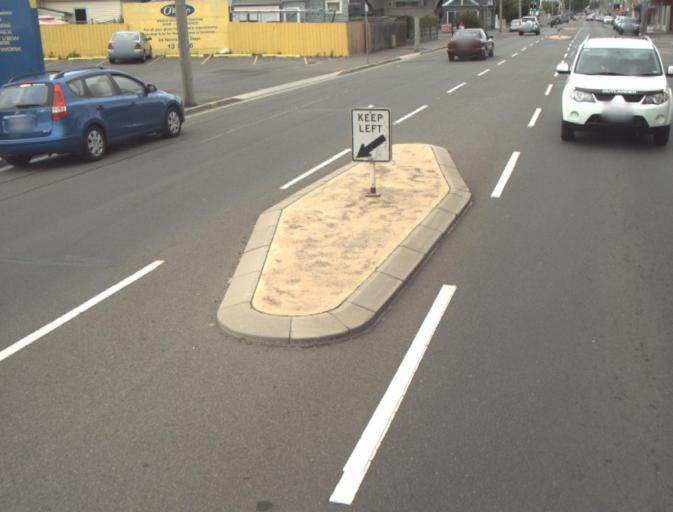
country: AU
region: Tasmania
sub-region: Launceston
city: Launceston
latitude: -41.4180
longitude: 147.1344
